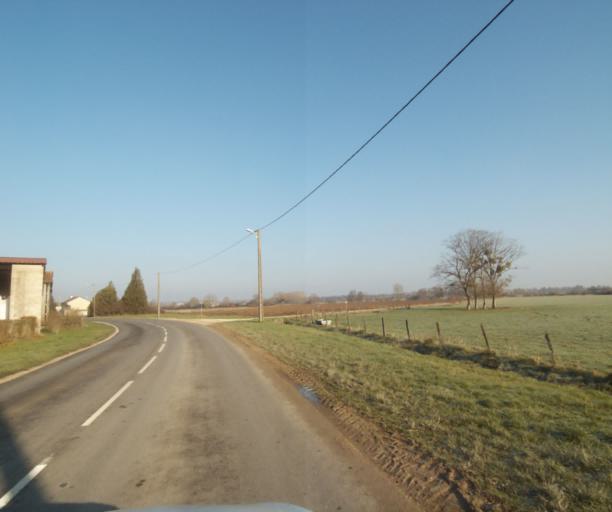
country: FR
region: Champagne-Ardenne
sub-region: Departement de la Haute-Marne
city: Montier-en-Der
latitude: 48.4574
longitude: 4.7695
